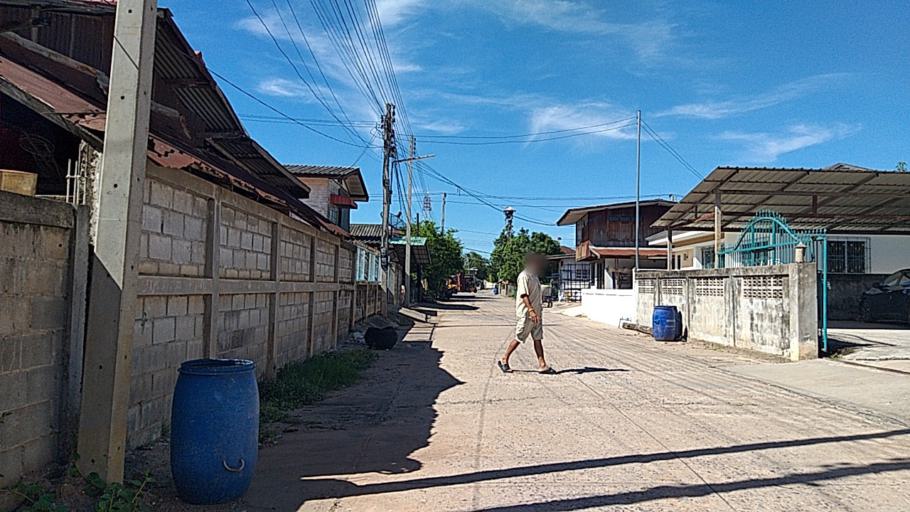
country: TH
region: Chaiyaphum
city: Ban Thaen
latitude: 16.4119
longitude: 102.3542
